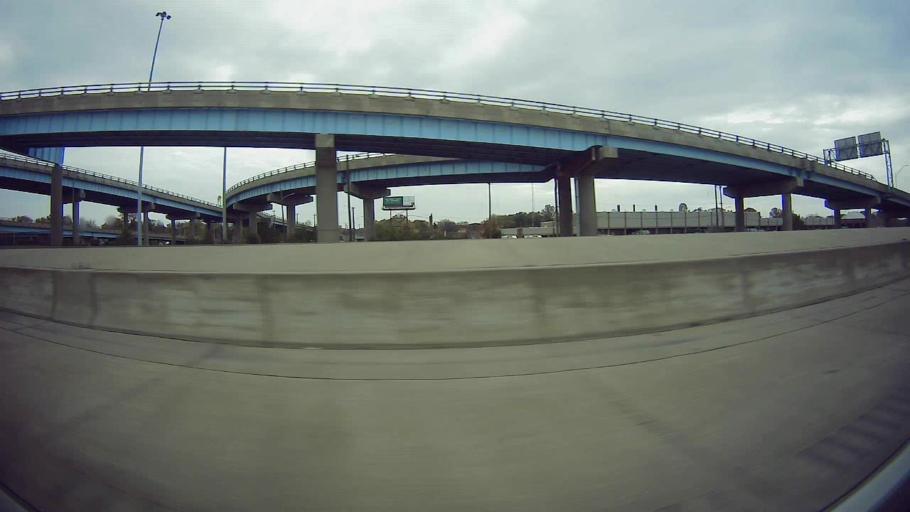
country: US
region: Michigan
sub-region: Wayne County
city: Dearborn Heights
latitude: 42.3781
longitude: -83.2217
